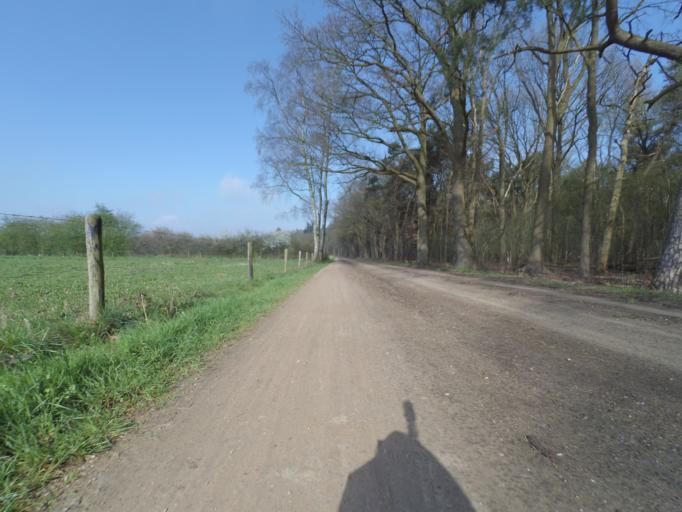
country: NL
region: Gelderland
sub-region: Gemeente Apeldoorn
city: Uddel
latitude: 52.2687
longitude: 5.7591
